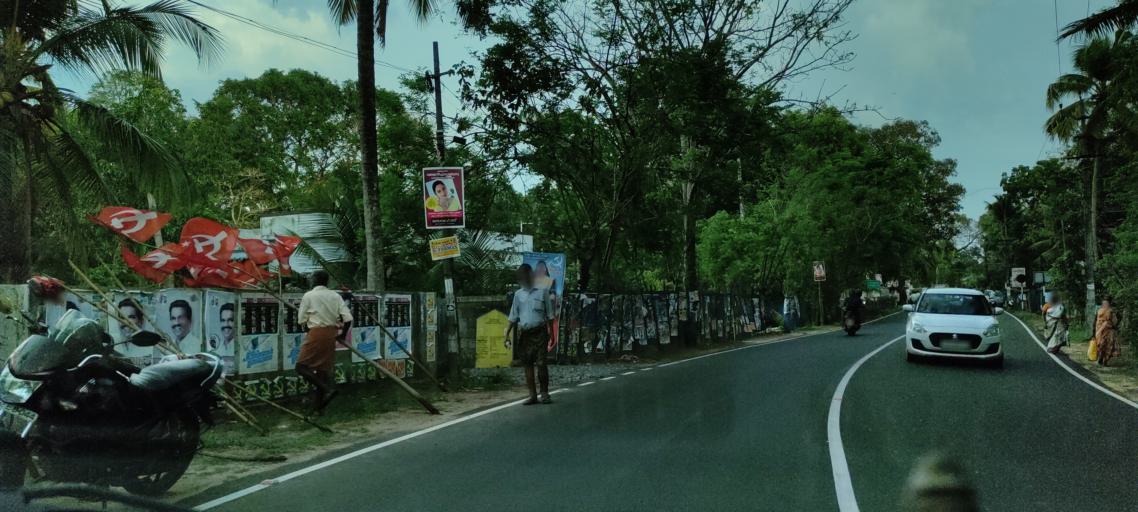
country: IN
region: Kerala
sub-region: Alappuzha
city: Kutiatodu
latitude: 9.8353
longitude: 76.3333
